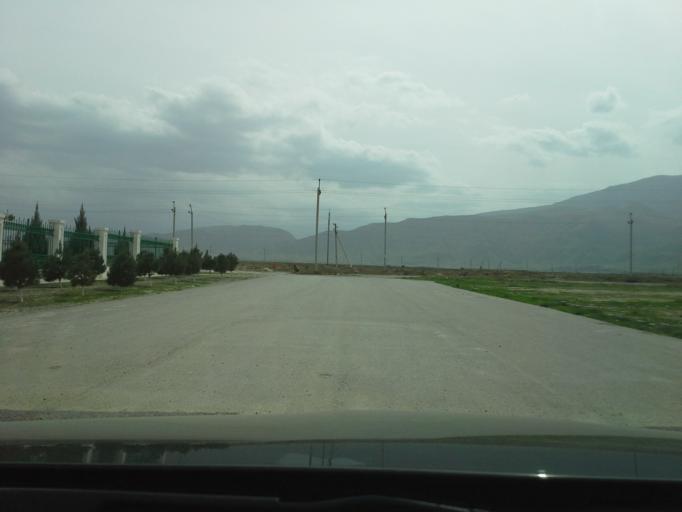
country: TM
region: Ahal
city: Abadan
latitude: 38.0518
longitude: 58.1400
